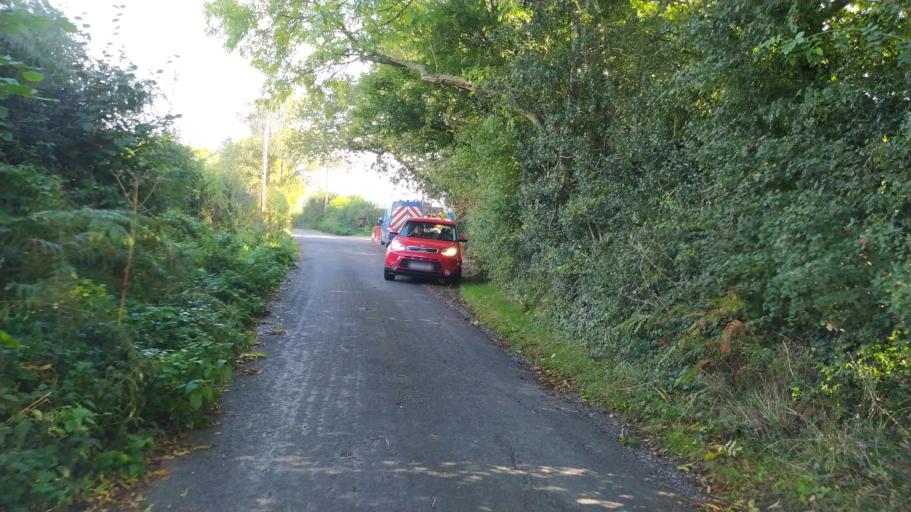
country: GB
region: England
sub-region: Wiltshire
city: Hindon
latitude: 51.0341
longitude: -2.1343
